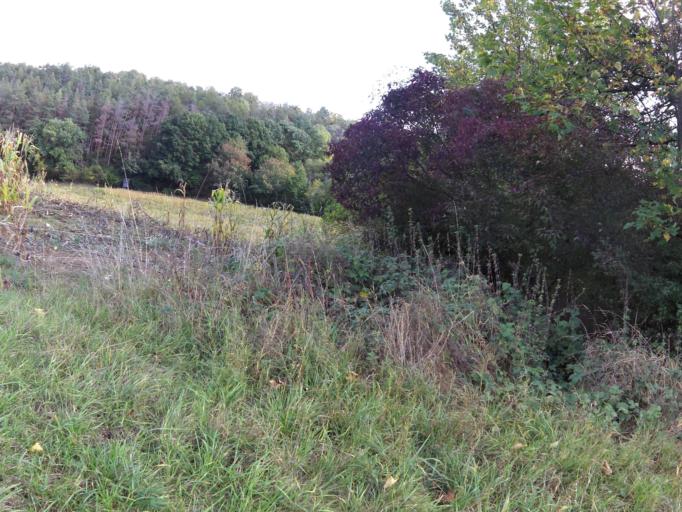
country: DE
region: Bavaria
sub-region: Regierungsbezirk Unterfranken
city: Erlabrunn
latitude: 49.8364
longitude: 9.8389
